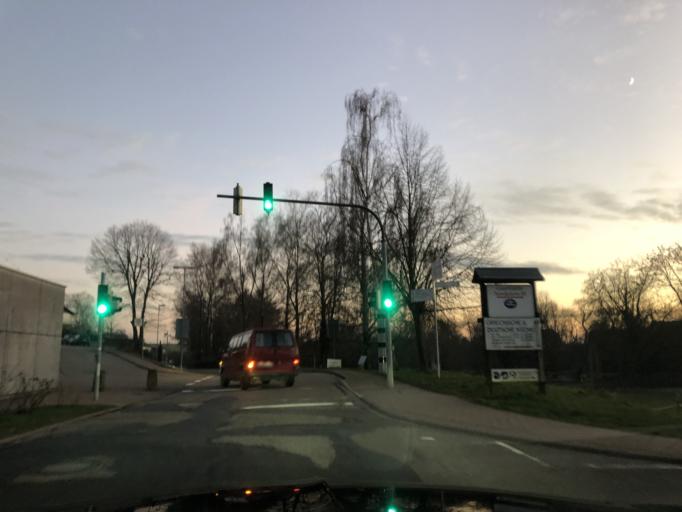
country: DE
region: Baden-Wuerttemberg
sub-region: Karlsruhe Region
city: Bammental
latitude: 49.3398
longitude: 8.7572
